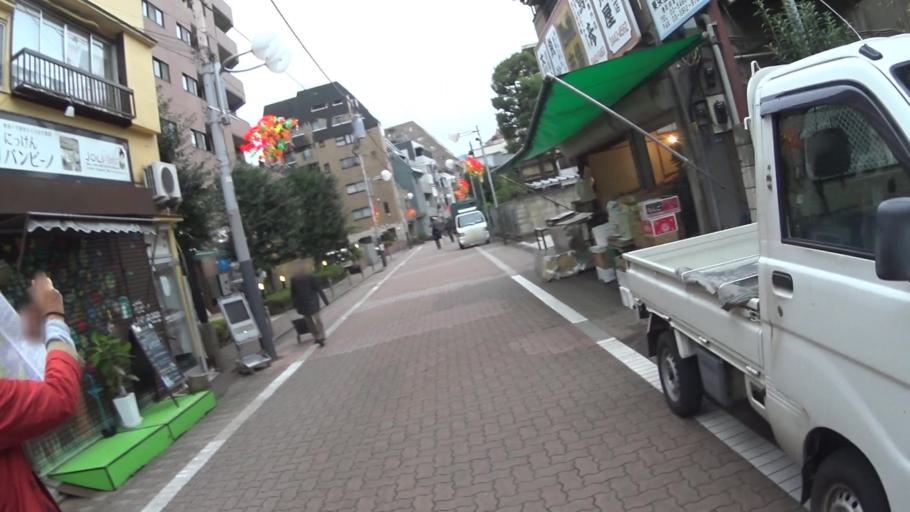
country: JP
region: Tokyo
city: Tokyo
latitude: 35.6451
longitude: 139.7315
